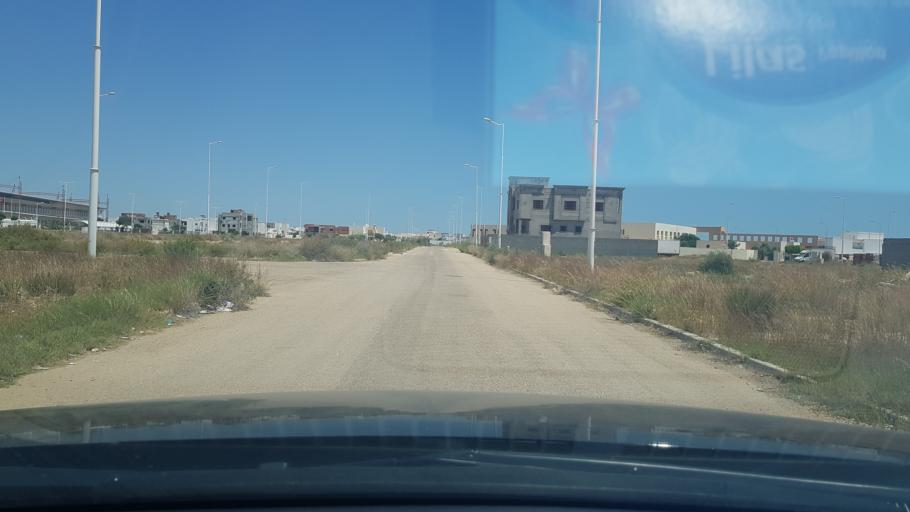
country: TN
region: Safaqis
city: Al Qarmadah
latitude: 34.8359
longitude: 10.7567
